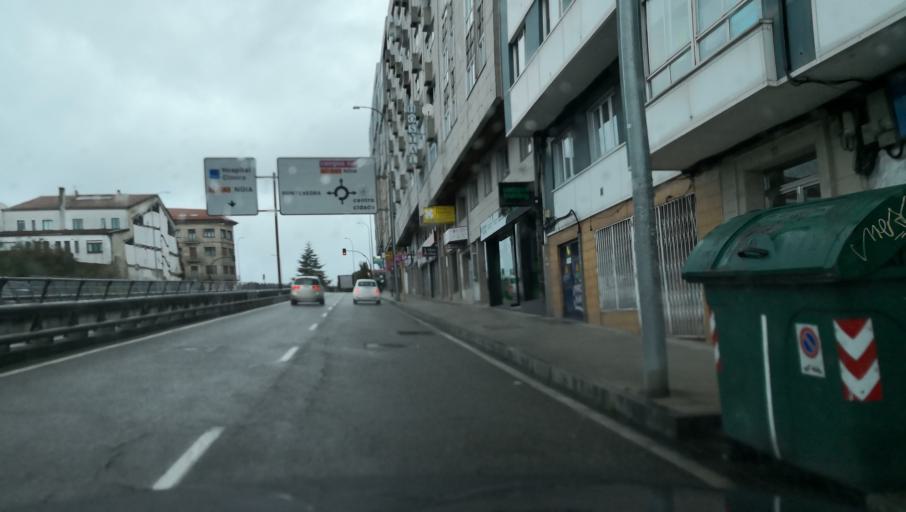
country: ES
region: Galicia
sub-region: Provincia da Coruna
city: Santiago de Compostela
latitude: 42.8724
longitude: -8.5521
